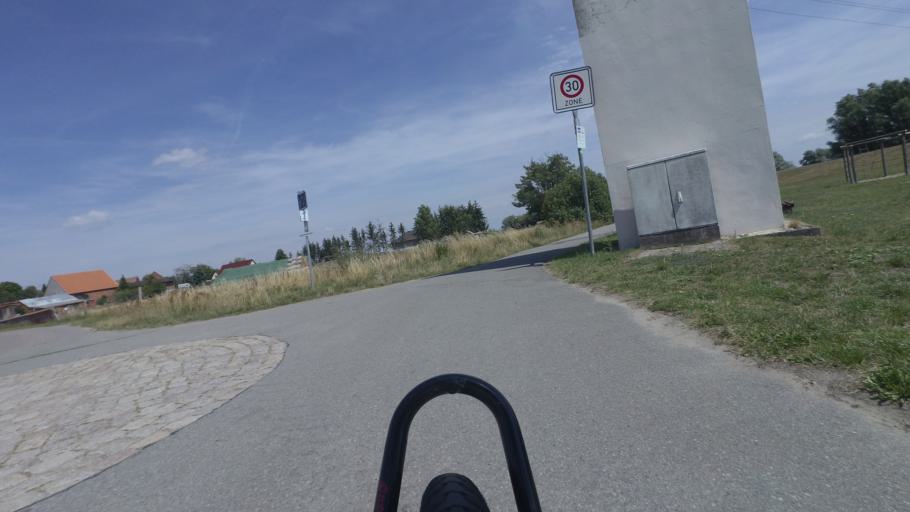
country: DE
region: Saxony-Anhalt
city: Kamern
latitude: 52.7810
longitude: 12.1979
